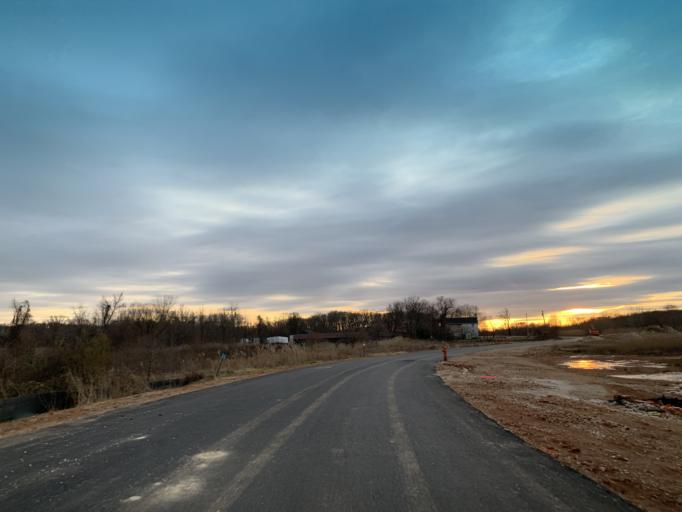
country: US
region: Maryland
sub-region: Baltimore County
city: Edgemere
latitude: 39.2342
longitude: -76.4266
